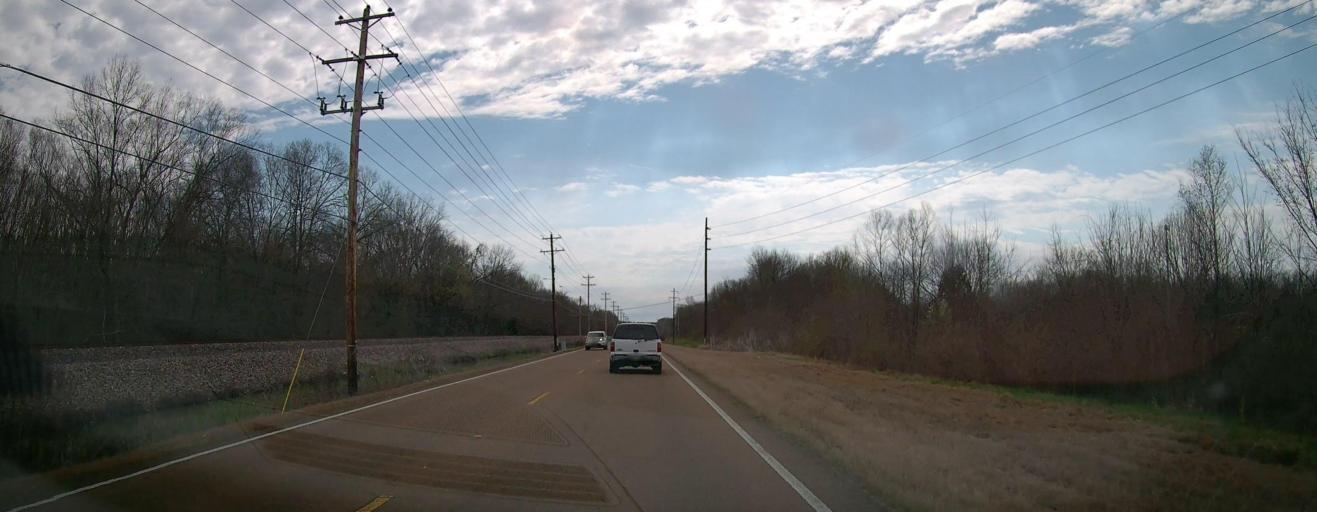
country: US
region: Mississippi
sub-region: Marshall County
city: Byhalia
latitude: 34.9105
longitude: -89.7579
